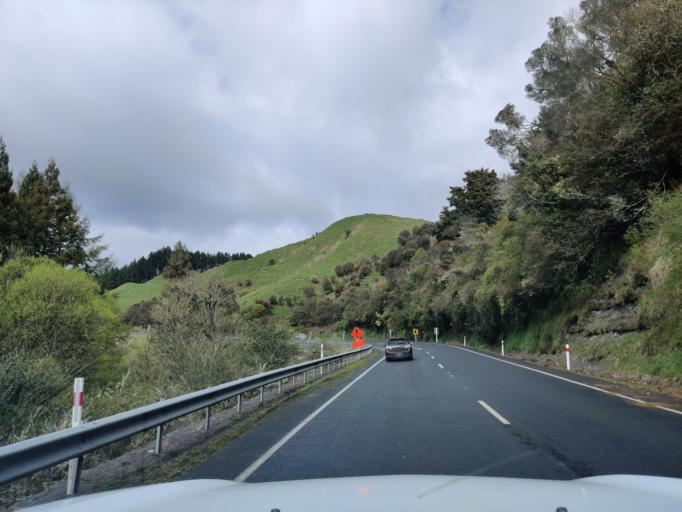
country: NZ
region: Waikato
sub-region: Otorohanga District
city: Otorohanga
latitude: -38.6082
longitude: 175.2171
